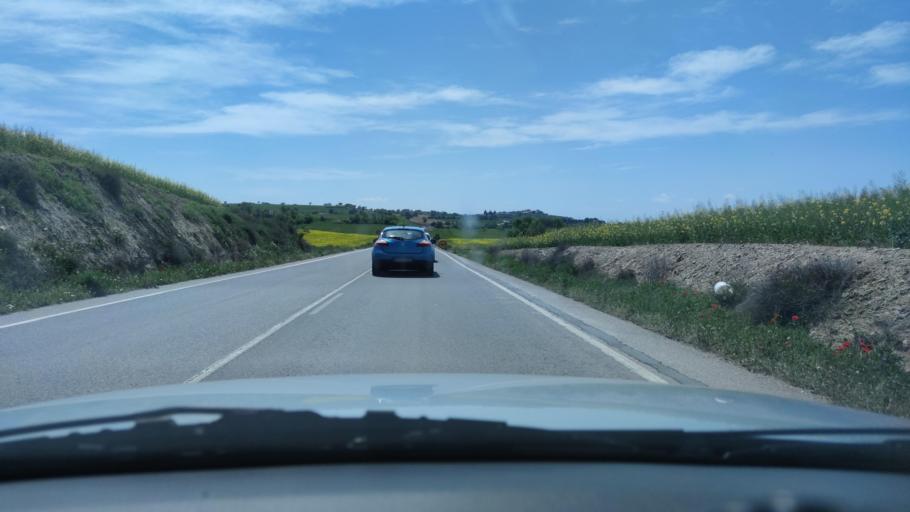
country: ES
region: Catalonia
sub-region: Provincia de Lleida
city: Mont-roig del Camp
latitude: 41.7772
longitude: 1.2673
